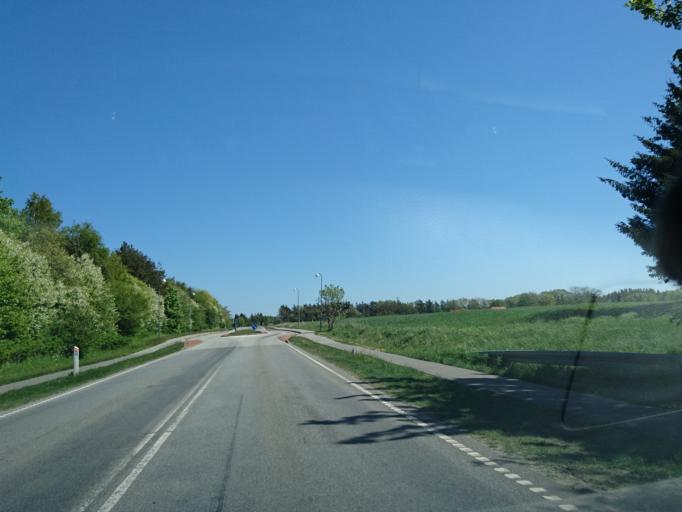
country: DK
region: North Denmark
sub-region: Hjorring Kommune
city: Sindal
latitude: 57.5813
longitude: 10.1886
